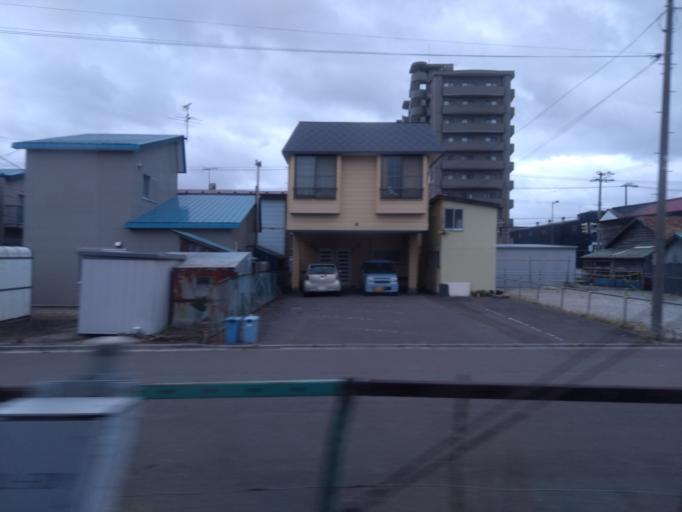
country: JP
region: Hokkaido
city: Hakodate
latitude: 41.7835
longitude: 140.7295
